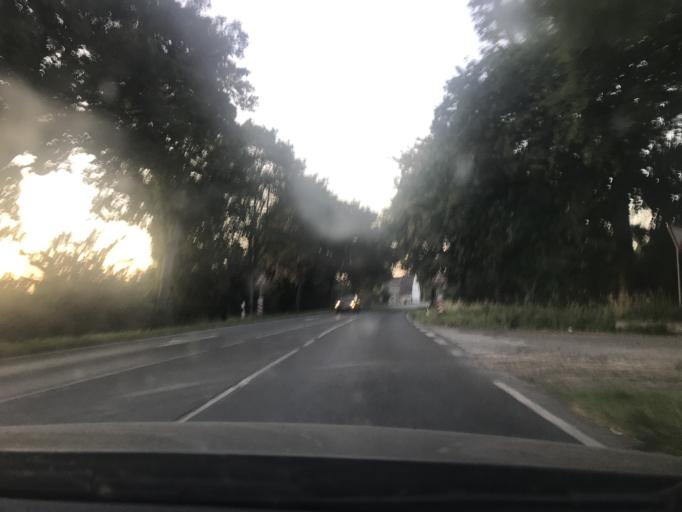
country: DE
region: North Rhine-Westphalia
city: Rheinberg
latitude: 51.5242
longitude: 6.6023
